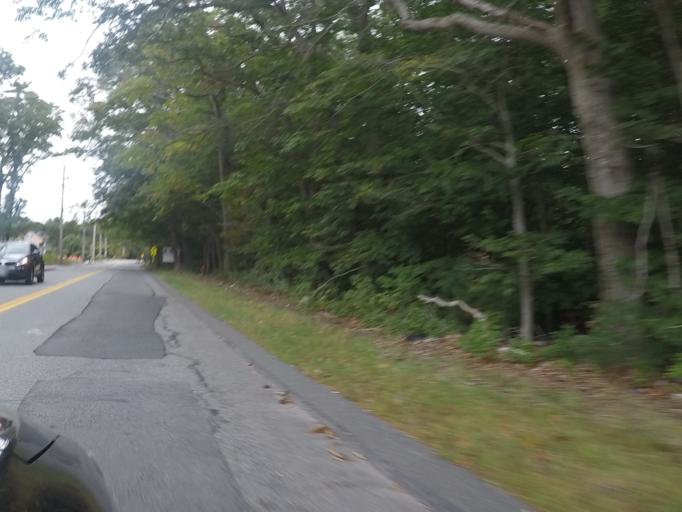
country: US
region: Massachusetts
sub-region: Bristol County
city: Smith Mills
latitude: 41.6457
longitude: -71.0073
